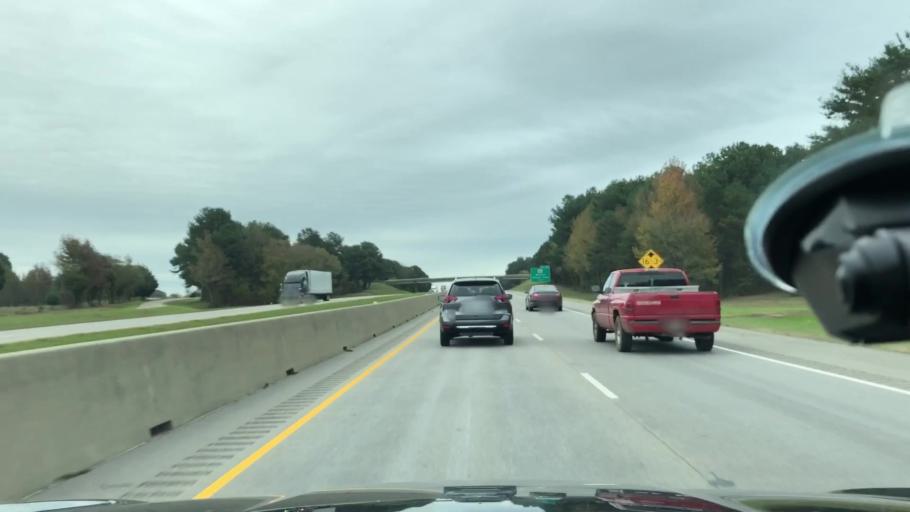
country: US
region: Texas
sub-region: Franklin County
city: Mount Vernon
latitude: 33.1613
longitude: -95.1361
